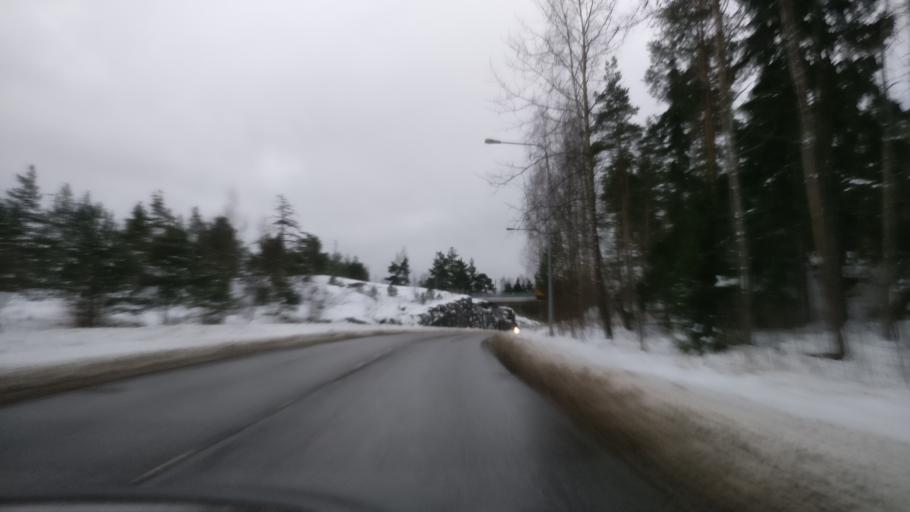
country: FI
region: Uusimaa
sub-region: Helsinki
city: Helsinki
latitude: 60.1741
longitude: 25.0497
